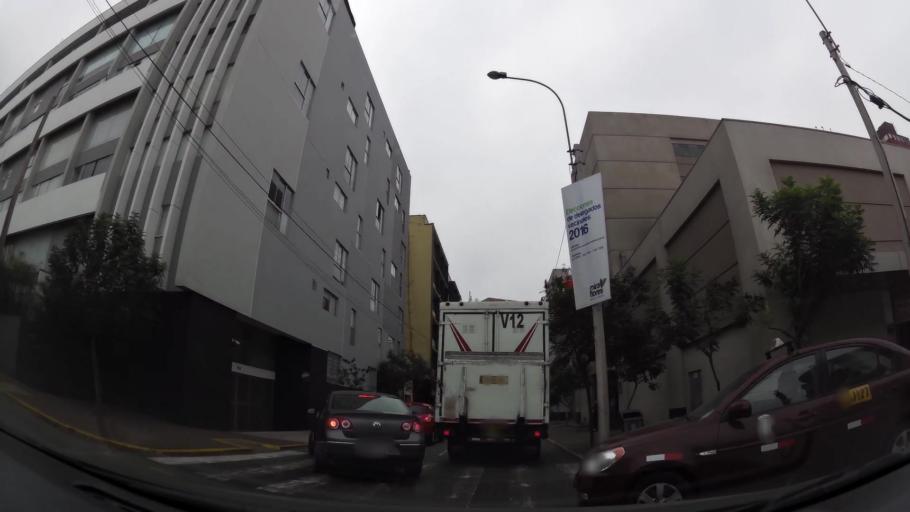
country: PE
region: Lima
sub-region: Lima
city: San Isidro
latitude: -12.1224
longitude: -77.0324
